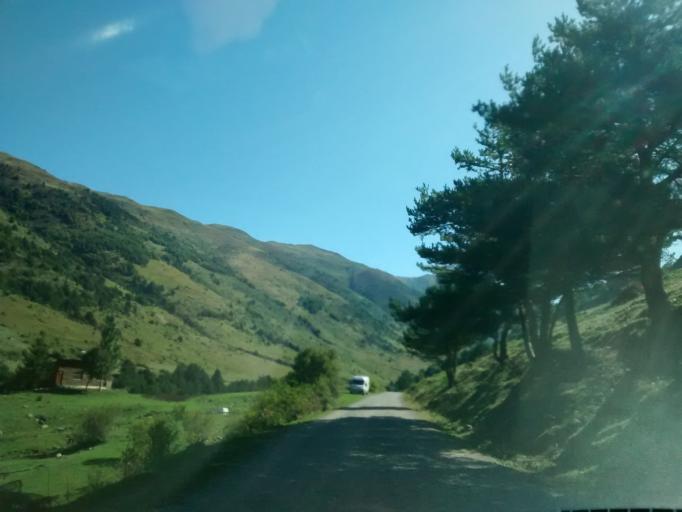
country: ES
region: Aragon
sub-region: Provincia de Huesca
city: Aragues del Puerto
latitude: 42.8533
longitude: -0.6895
